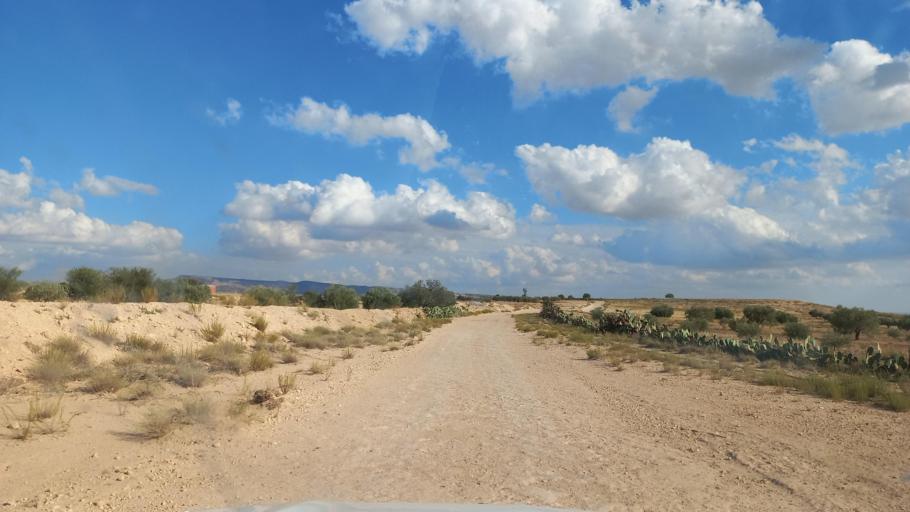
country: TN
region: Al Qasrayn
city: Sbiba
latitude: 35.3970
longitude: 9.0384
